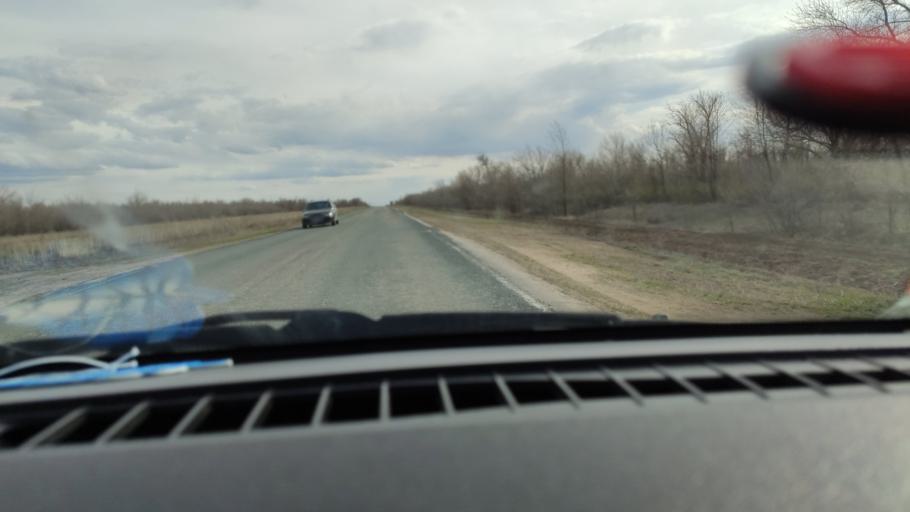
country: RU
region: Saratov
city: Rovnoye
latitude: 50.9717
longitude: 46.1170
